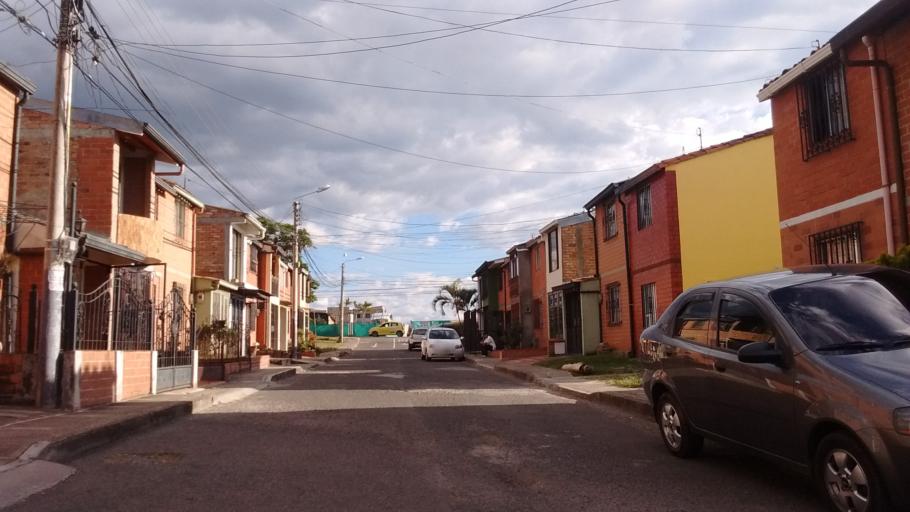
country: CO
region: Cauca
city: Popayan
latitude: 2.4860
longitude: -76.5823
